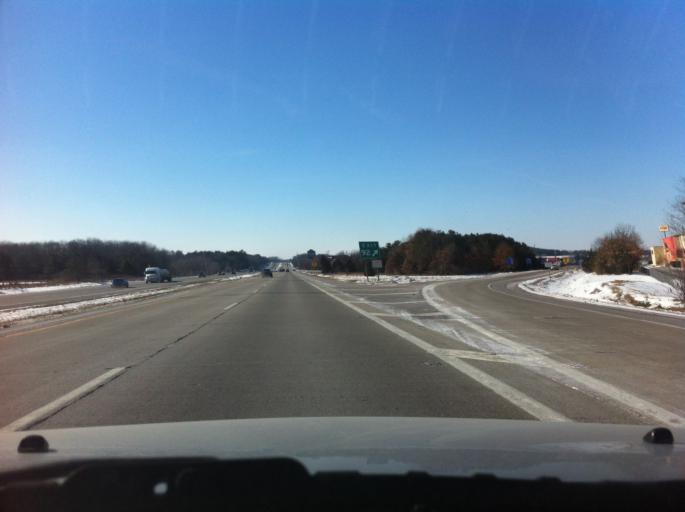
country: US
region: Wisconsin
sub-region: Columbia County
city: Wisconsin Dells
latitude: 43.5593
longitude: -89.7182
